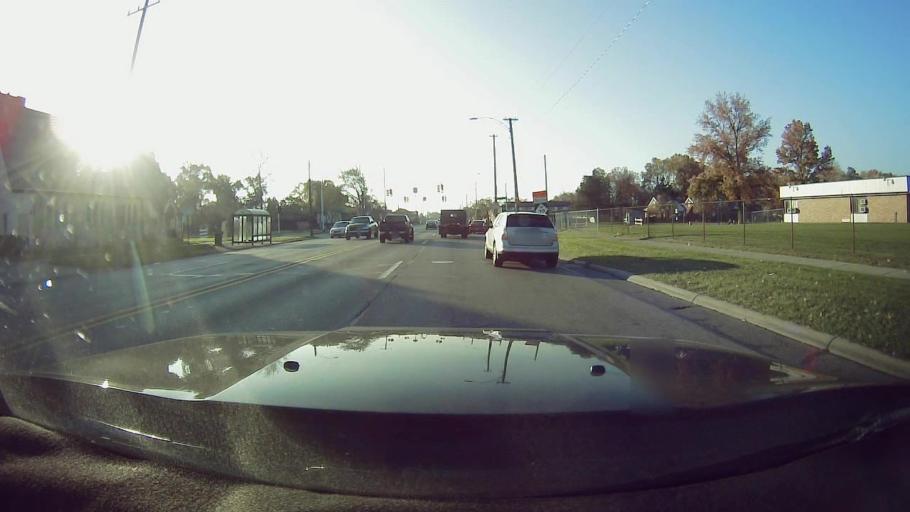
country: US
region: Michigan
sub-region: Oakland County
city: Oak Park
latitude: 42.4202
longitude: -83.1996
